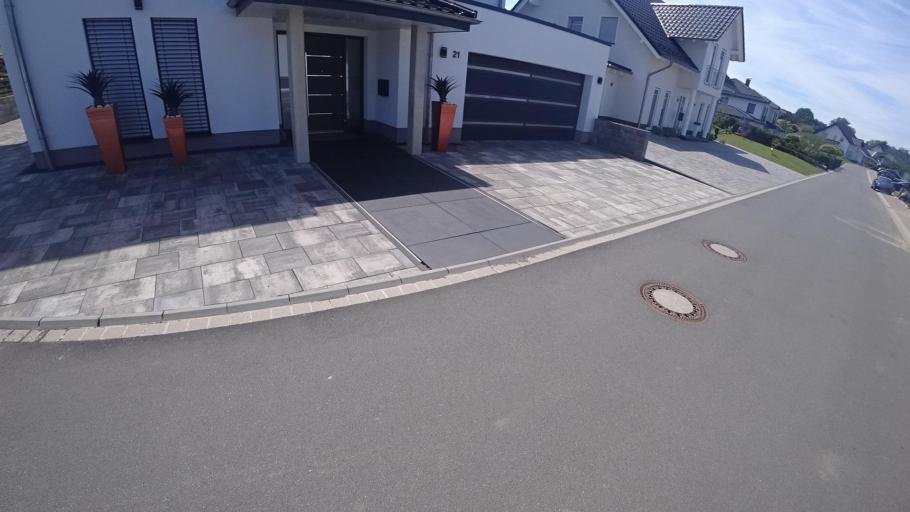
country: DE
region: Rheinland-Pfalz
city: Mammelzen
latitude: 50.6978
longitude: 7.6618
